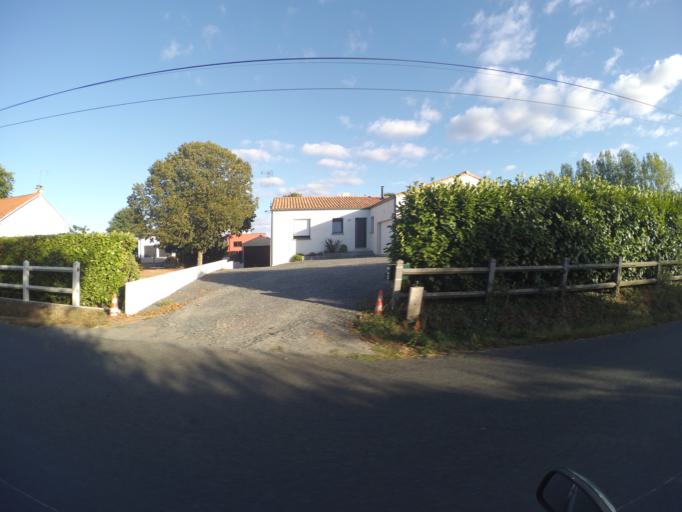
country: FR
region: Pays de la Loire
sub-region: Departement de la Vendee
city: Saint-Hilaire-de-Loulay
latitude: 46.9943
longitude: -1.3465
